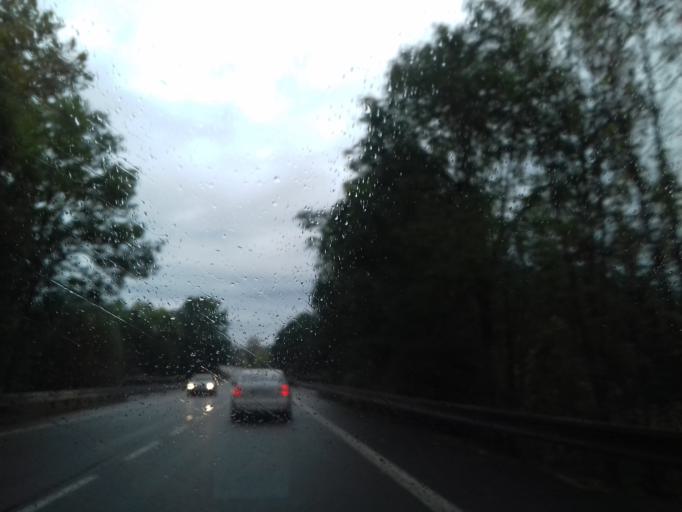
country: CZ
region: Pardubicky
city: Horni Jeleni
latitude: 49.9996
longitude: 16.1028
